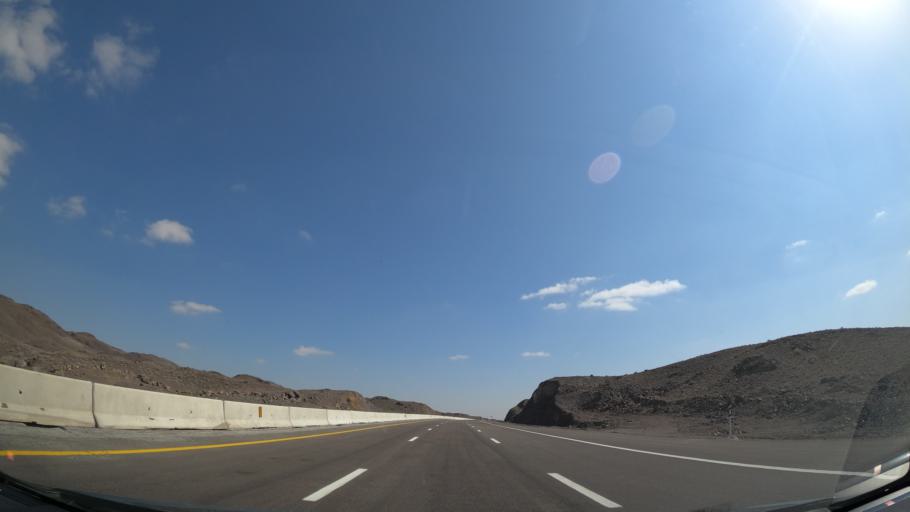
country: IR
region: Alborz
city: Nazarabad
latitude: 35.6607
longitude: 50.6575
